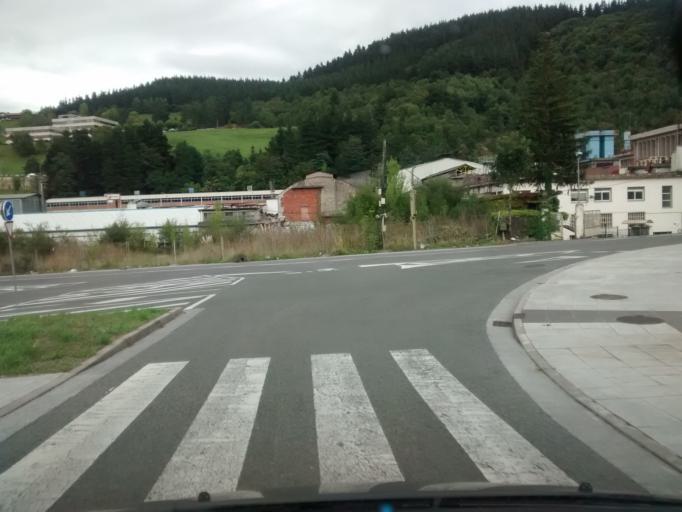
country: ES
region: Basque Country
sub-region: Provincia de Guipuzcoa
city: Arrasate / Mondragon
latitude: 43.0622
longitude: -2.5039
